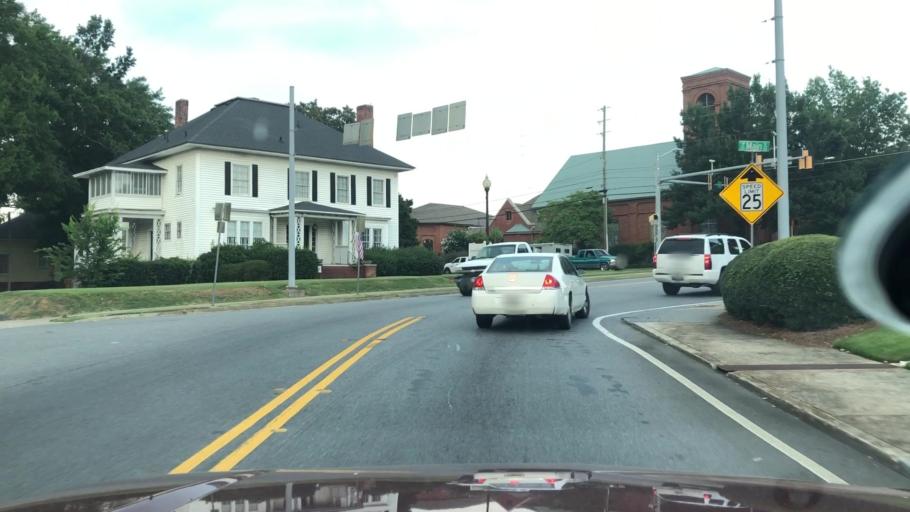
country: US
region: Georgia
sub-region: Bartow County
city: Cartersville
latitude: 34.1637
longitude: -84.8005
